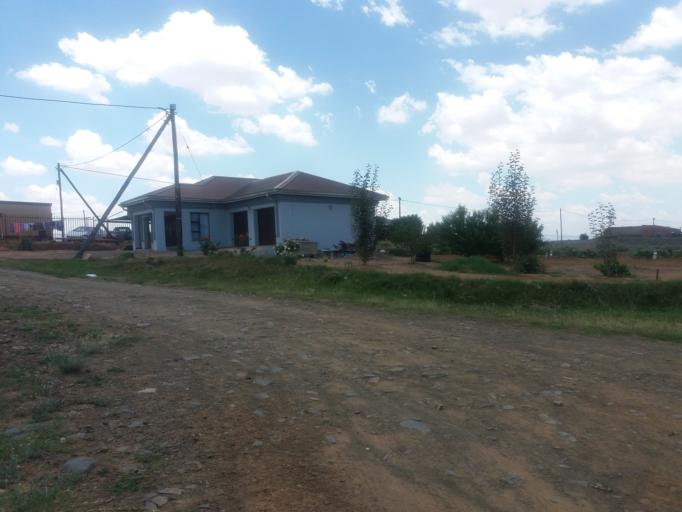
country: LS
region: Maseru
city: Maseru
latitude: -29.3679
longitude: 27.4739
